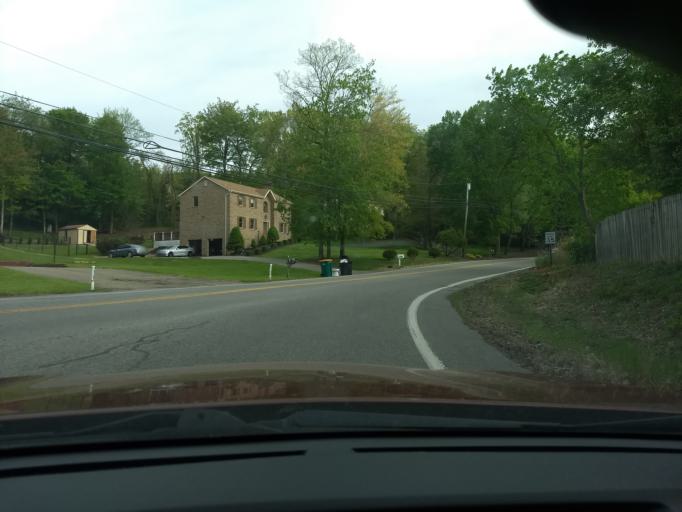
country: US
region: Pennsylvania
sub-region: Allegheny County
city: Allison Park
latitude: 40.5971
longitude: -79.9305
